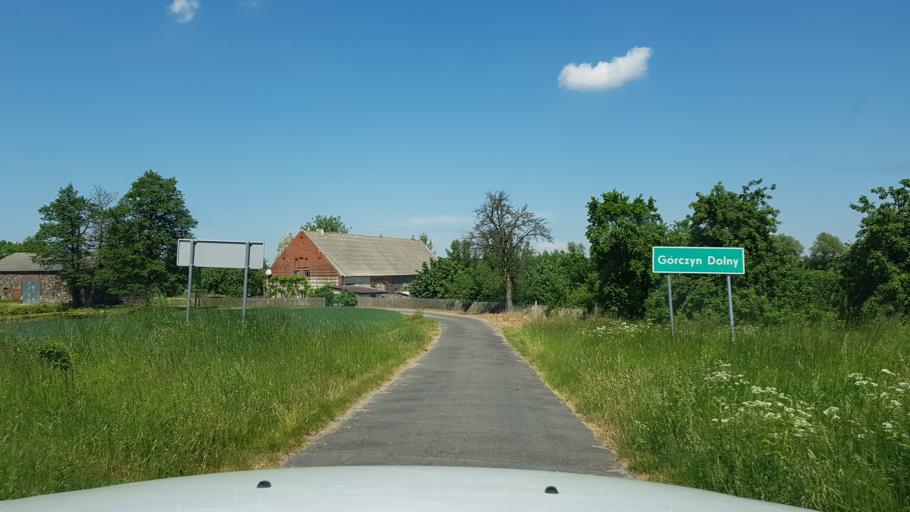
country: PL
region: West Pomeranian Voivodeship
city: Trzcinsko Zdroj
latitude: 52.9312
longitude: 14.5817
